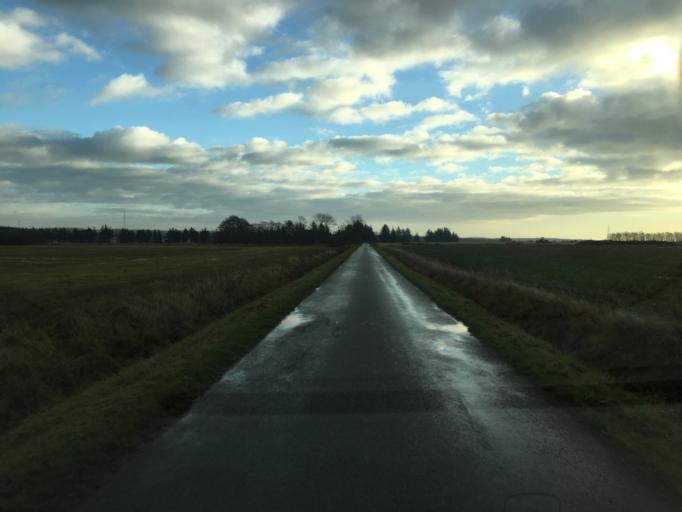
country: DK
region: South Denmark
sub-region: Tonder Kommune
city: Sherrebek
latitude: 55.1352
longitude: 8.8321
